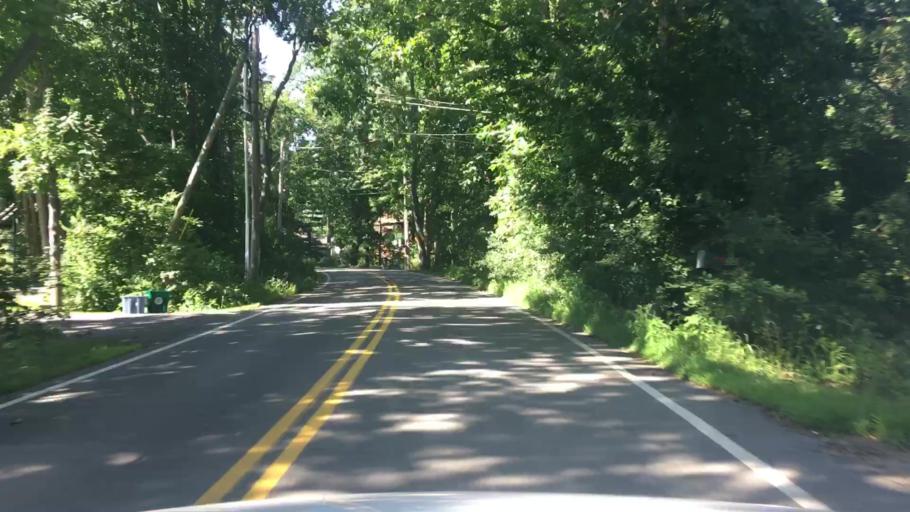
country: US
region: New Hampshire
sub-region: Strafford County
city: Dover
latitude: 43.1787
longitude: -70.8376
